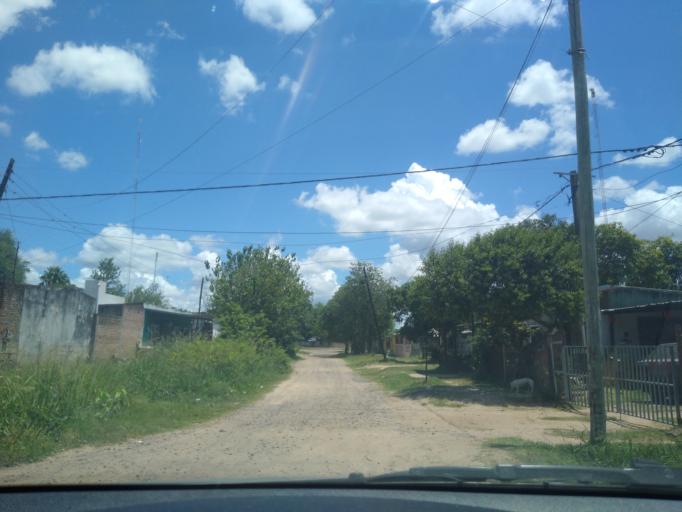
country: AR
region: Chaco
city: Barranqueras
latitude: -27.4742
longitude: -58.9335
